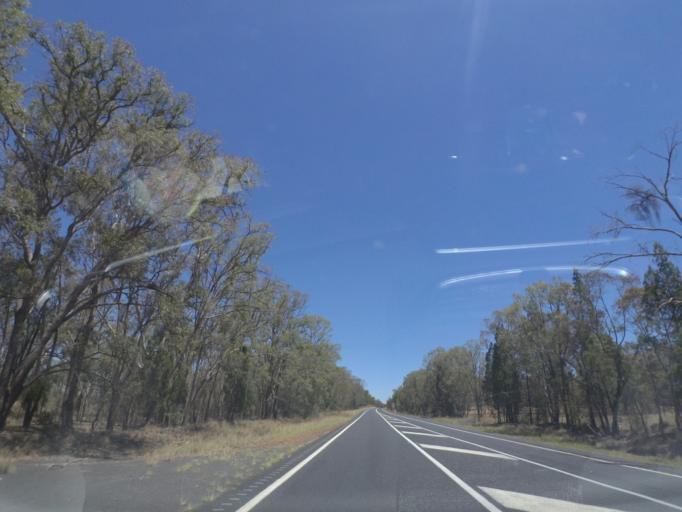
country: AU
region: New South Wales
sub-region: Warrumbungle Shire
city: Coonabarabran
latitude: -31.2262
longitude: 149.3221
